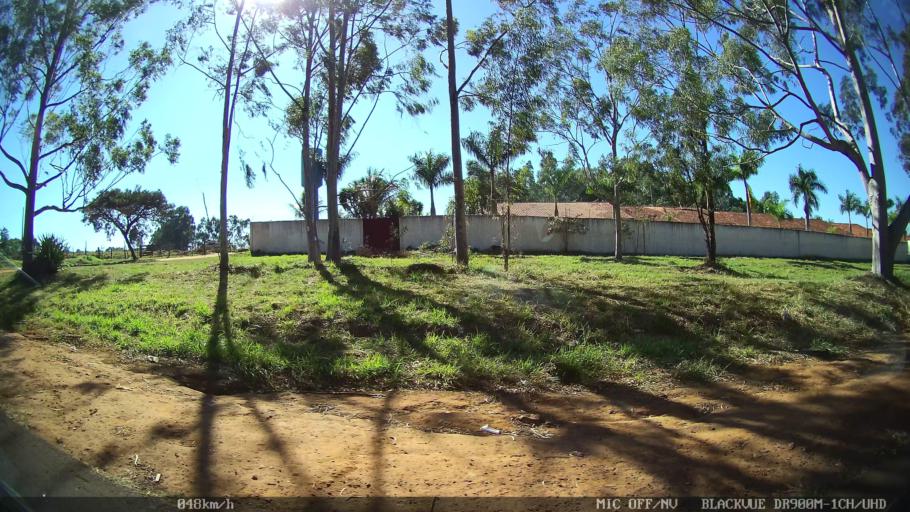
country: BR
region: Sao Paulo
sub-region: Franca
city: Franca
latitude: -20.5761
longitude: -47.3461
